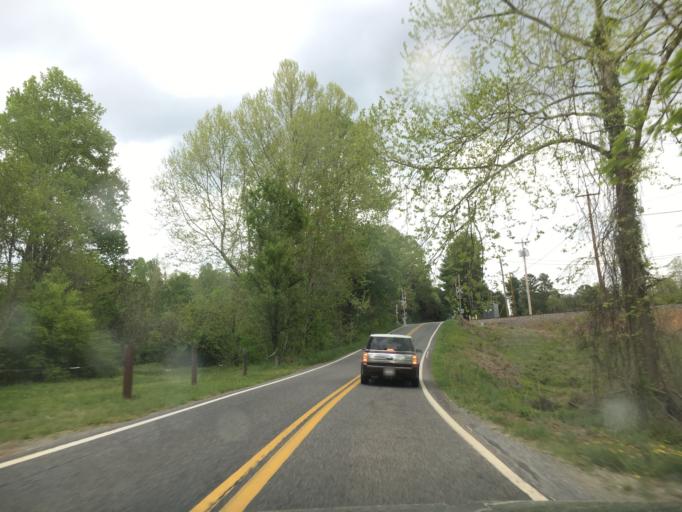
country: US
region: Virginia
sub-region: Campbell County
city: Rustburg
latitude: 37.3312
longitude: -79.1133
